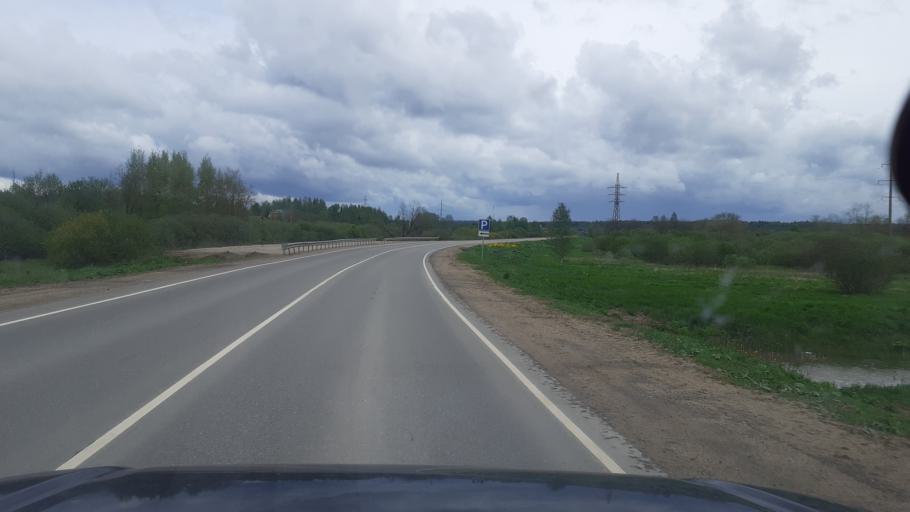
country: RU
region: Moskovskaya
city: Sychevo
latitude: 55.9870
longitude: 36.2213
